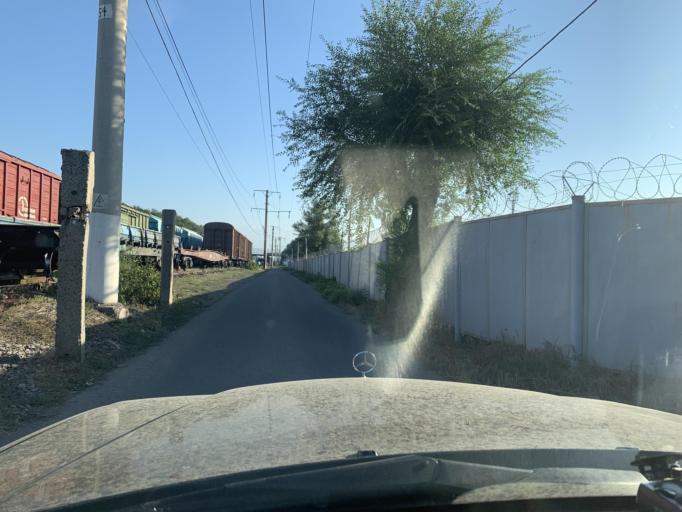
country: KZ
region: Almaty Oblysy
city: Energeticheskiy
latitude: 43.3883
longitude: 76.9988
